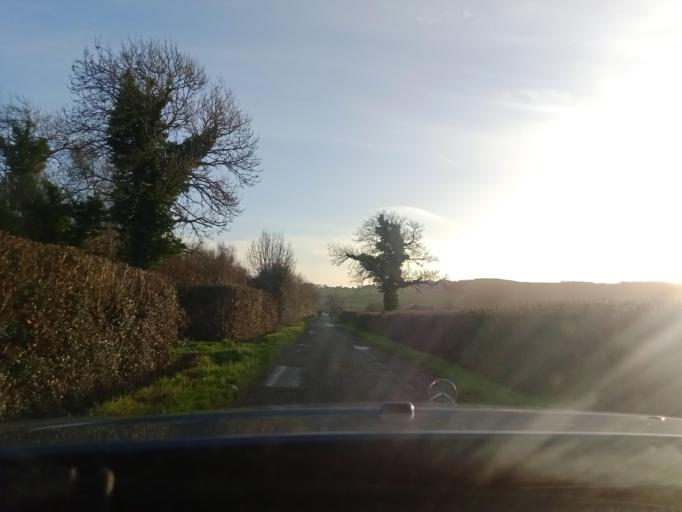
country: IE
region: Leinster
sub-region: Kilkenny
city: Callan
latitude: 52.4779
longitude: -7.4623
